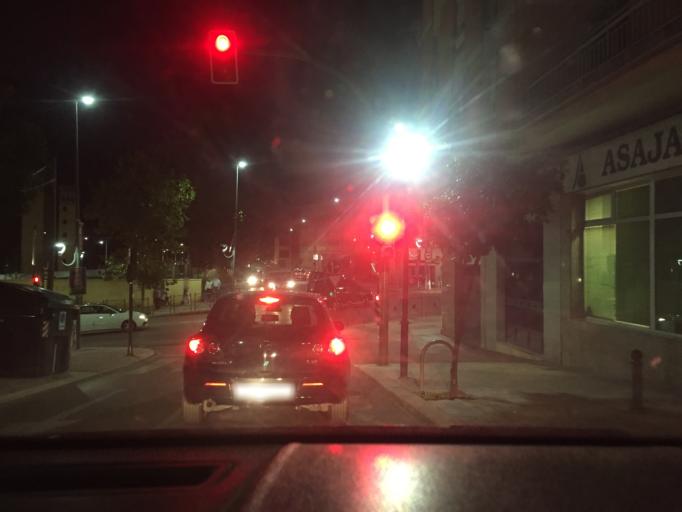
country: ES
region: Andalusia
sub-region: Provincia de Jaen
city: Jaen
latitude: 37.7692
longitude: -3.7834
